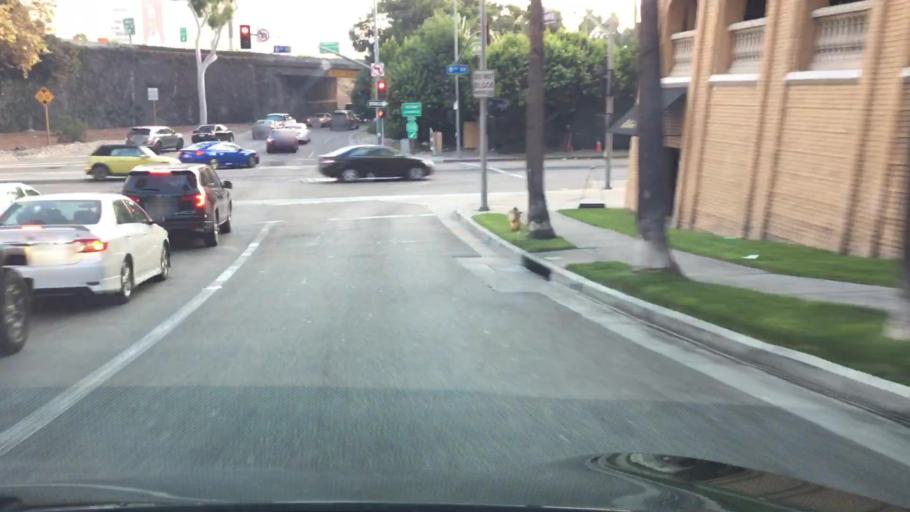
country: US
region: California
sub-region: Los Angeles County
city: Los Angeles
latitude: 34.0499
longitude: -118.2648
